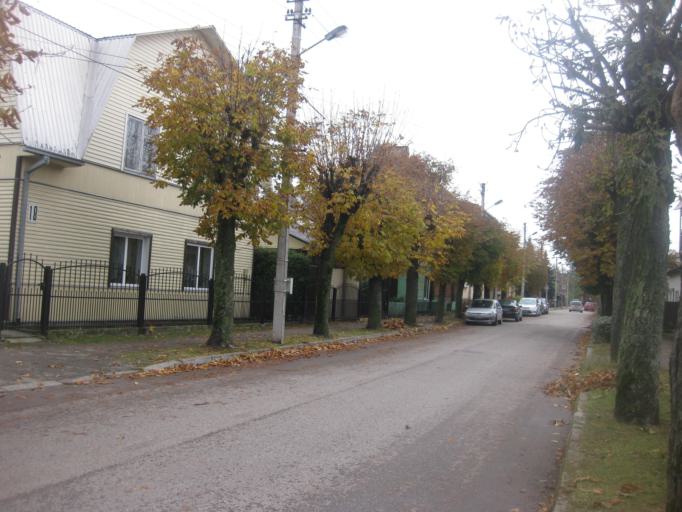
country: LT
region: Kauno apskritis
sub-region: Kaunas
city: Kaunas
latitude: 54.9091
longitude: 23.9218
